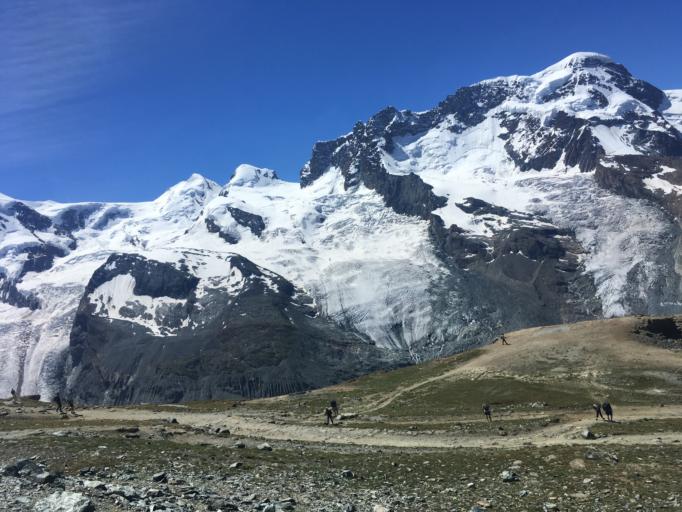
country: CH
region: Valais
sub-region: Visp District
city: Zermatt
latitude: 45.9831
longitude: 7.7794
